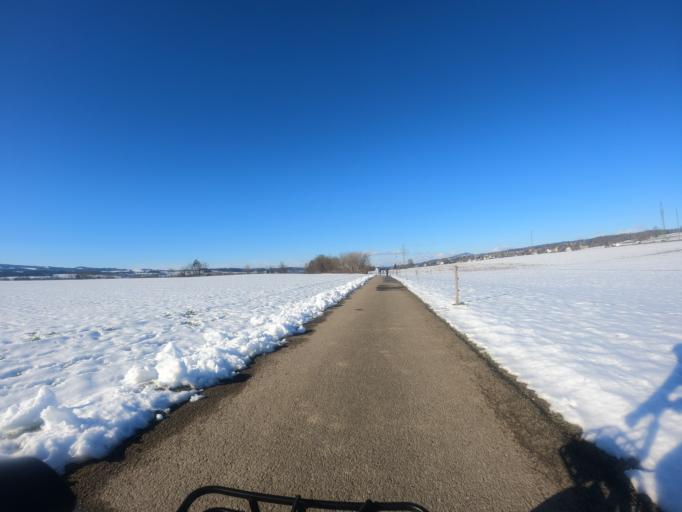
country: CH
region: Zurich
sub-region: Bezirk Affoltern
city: Ottenbach
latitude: 47.2873
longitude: 8.3976
